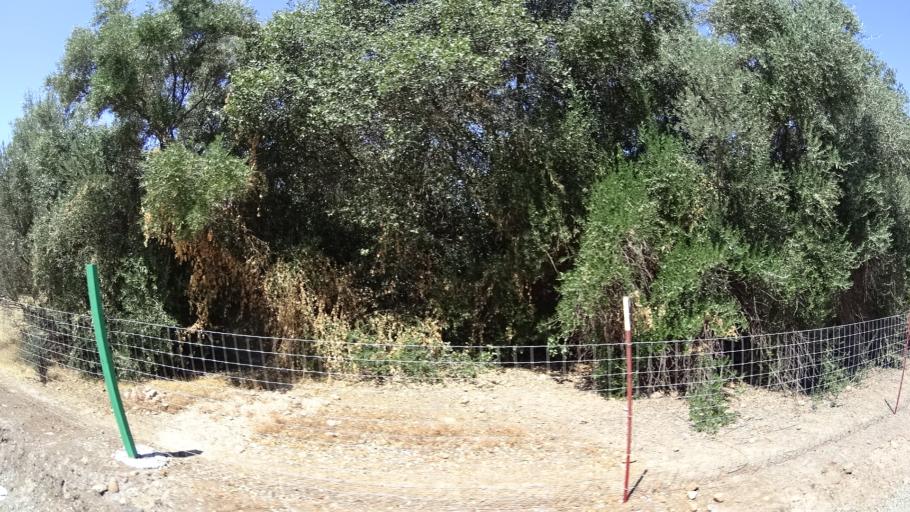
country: US
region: California
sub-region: Calaveras County
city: Rancho Calaveras
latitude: 38.1356
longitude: -120.9133
